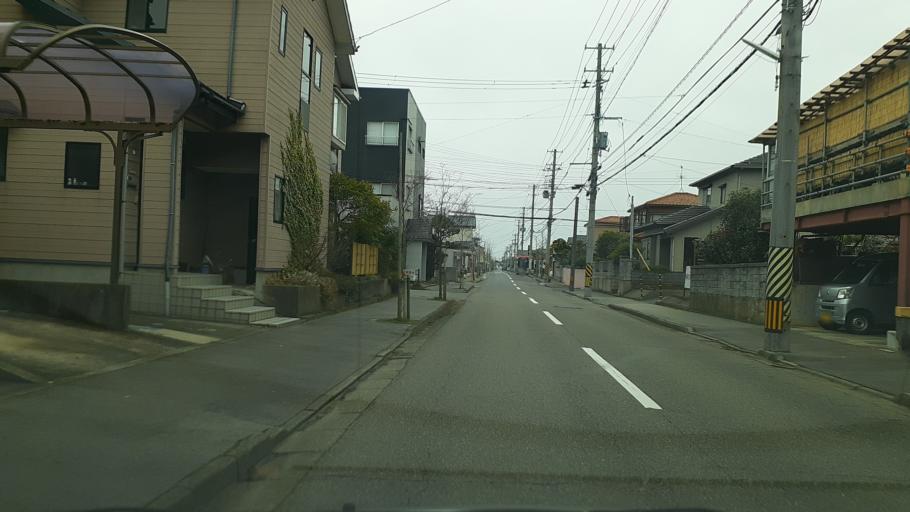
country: JP
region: Niigata
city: Niigata-shi
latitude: 37.8643
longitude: 139.0413
